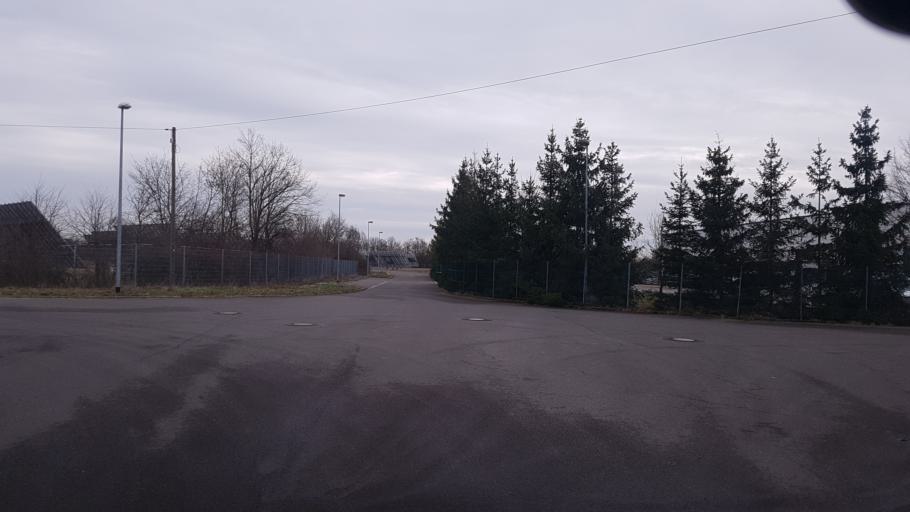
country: DE
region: Brandenburg
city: Sonnewalde
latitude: 51.6765
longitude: 13.6472
